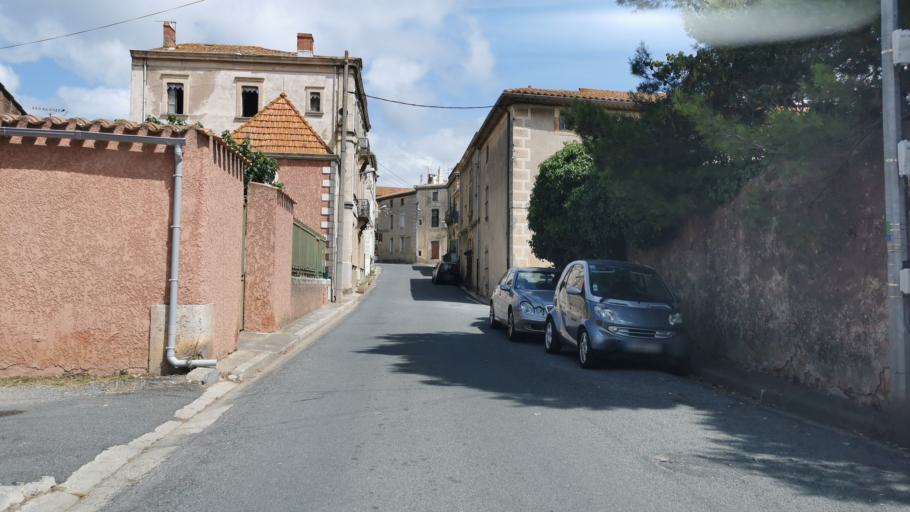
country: FR
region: Languedoc-Roussillon
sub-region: Departement de l'Aude
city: Bizanet
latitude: 43.1627
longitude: 2.8693
